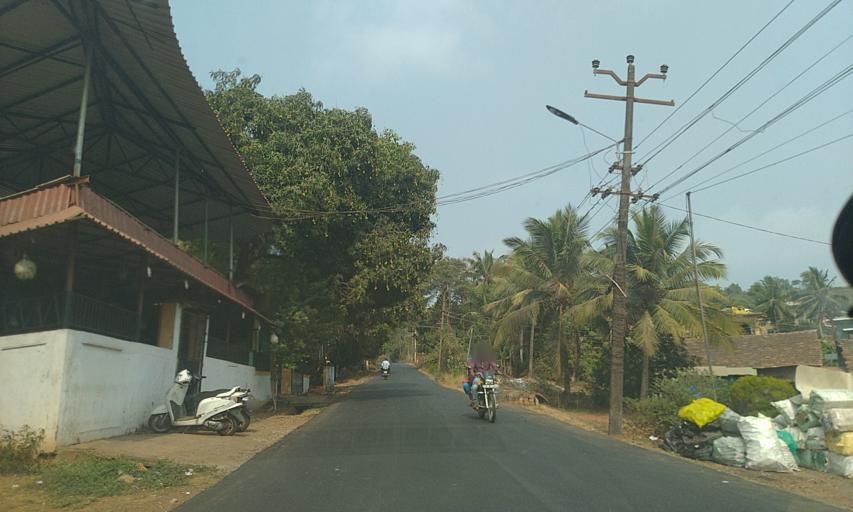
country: IN
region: Goa
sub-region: South Goa
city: Raia
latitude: 15.3078
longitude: 73.9752
